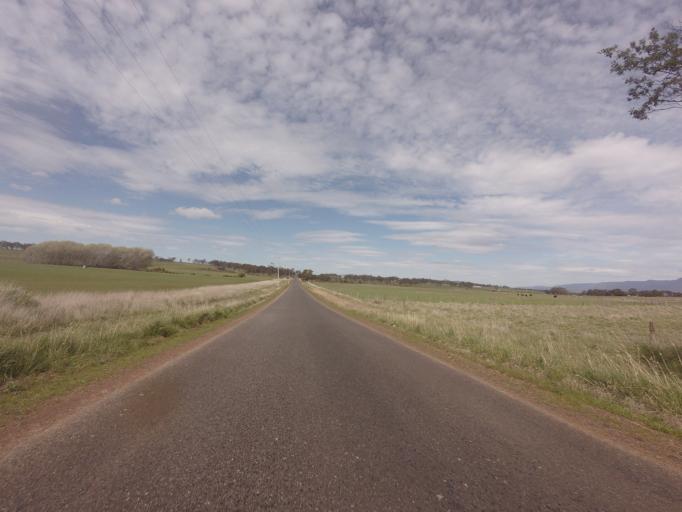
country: AU
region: Tasmania
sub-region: Northern Midlands
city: Longford
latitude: -41.7781
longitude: 147.2280
